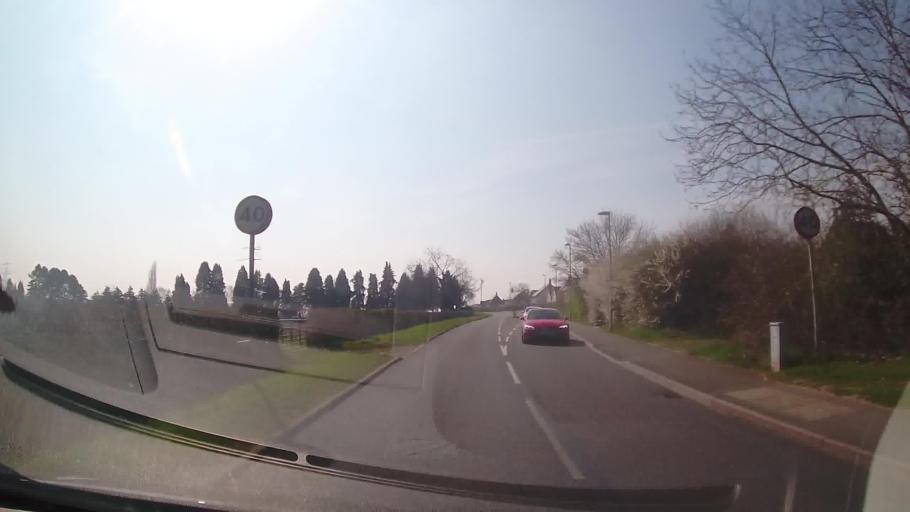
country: GB
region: England
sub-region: Leicestershire
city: Anstey
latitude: 52.6695
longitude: -1.1936
